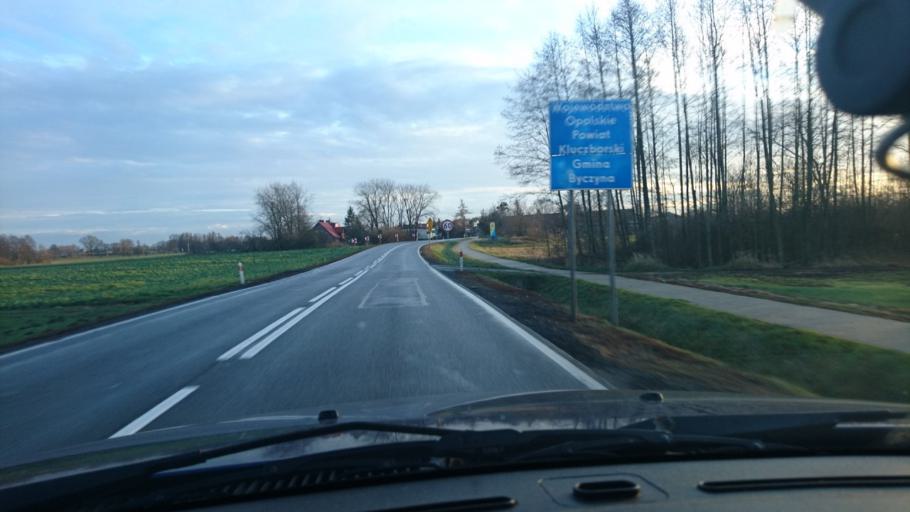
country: PL
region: Greater Poland Voivodeship
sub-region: Powiat kepinski
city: Opatow
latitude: 51.1714
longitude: 18.1462
